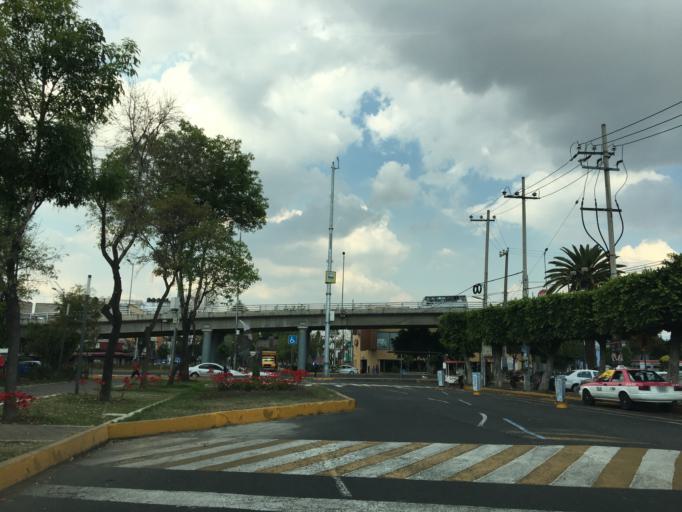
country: MX
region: Mexico City
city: Mexico City
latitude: 19.4201
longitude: -99.1150
